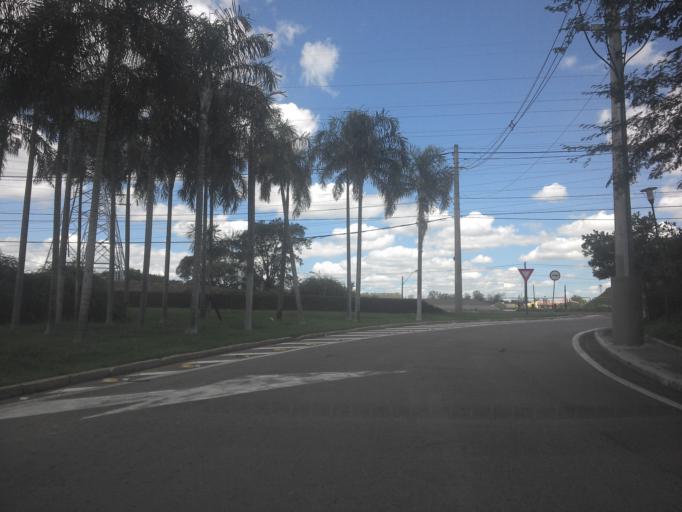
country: BR
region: Sao Paulo
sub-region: Campinas
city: Campinas
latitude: -22.8935
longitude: -47.0249
